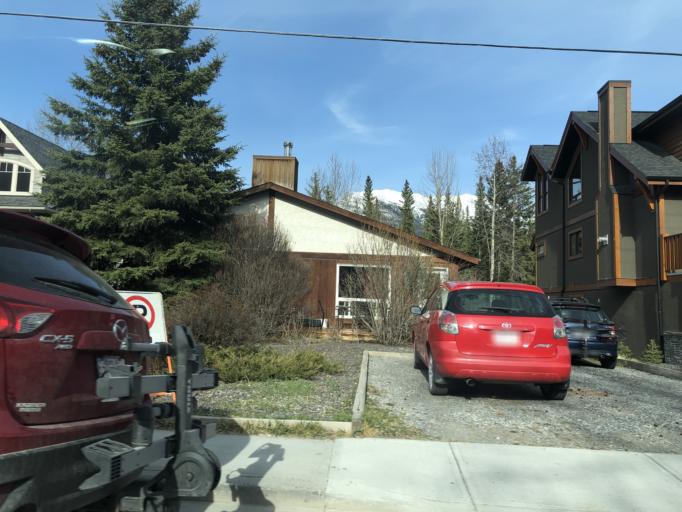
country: CA
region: Alberta
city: Canmore
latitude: 51.0837
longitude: -115.3671
